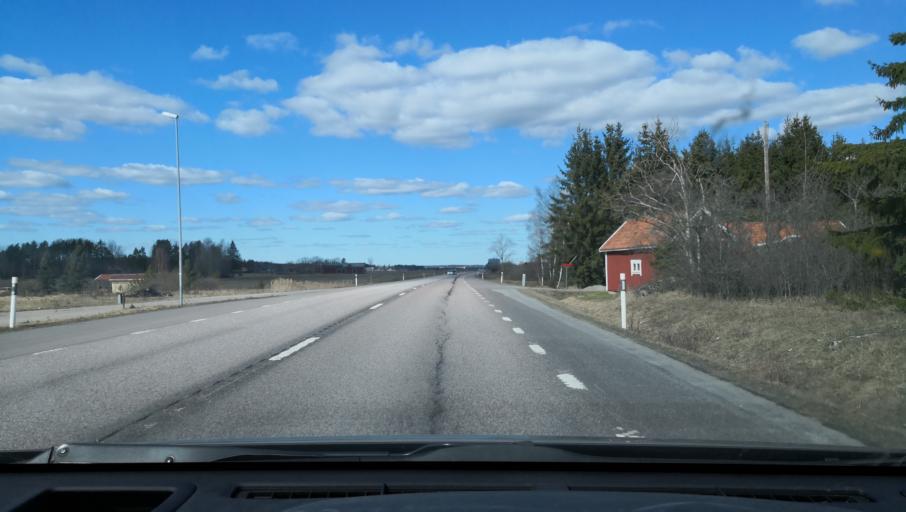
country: SE
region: Vaestmanland
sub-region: Sala Kommun
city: Sala
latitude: 59.8730
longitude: 16.6270
